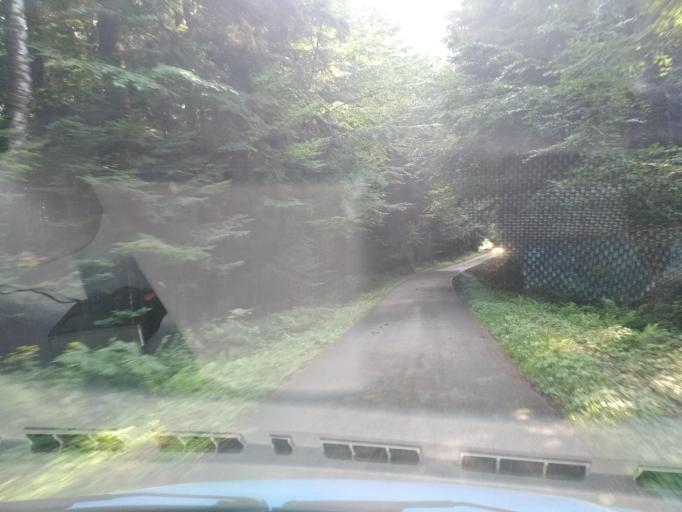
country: PL
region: Subcarpathian Voivodeship
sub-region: Powiat strzyzowski
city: Polomia
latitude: 49.8962
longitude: 21.9115
